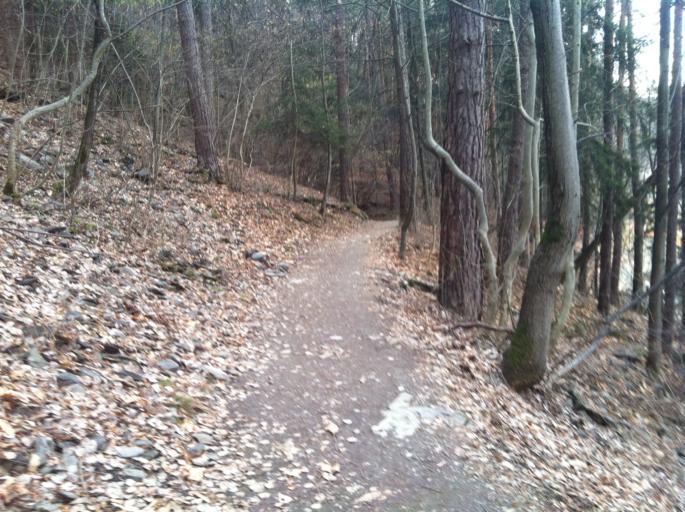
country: IT
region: Trentino-Alto Adige
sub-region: Bolzano
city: Bressanone
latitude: 46.7035
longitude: 11.6663
